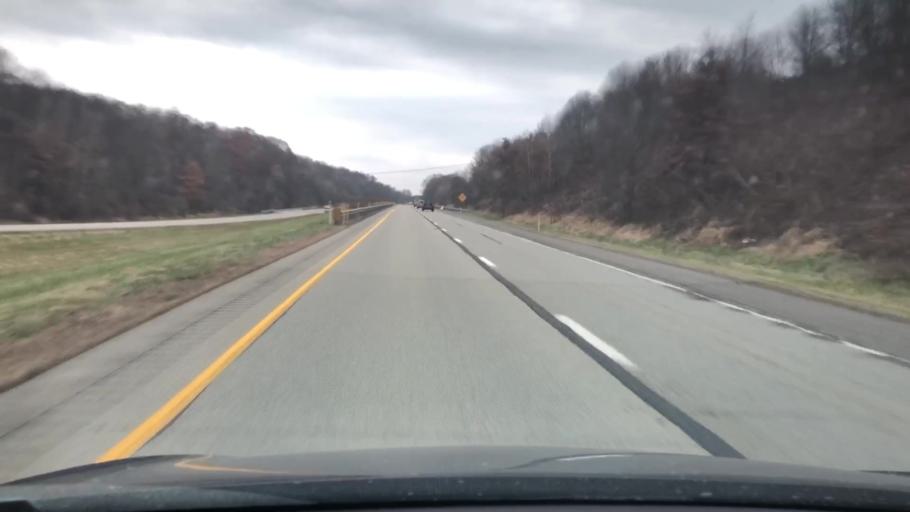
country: US
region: Pennsylvania
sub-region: Armstrong County
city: West Hills
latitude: 40.7999
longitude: -79.5696
